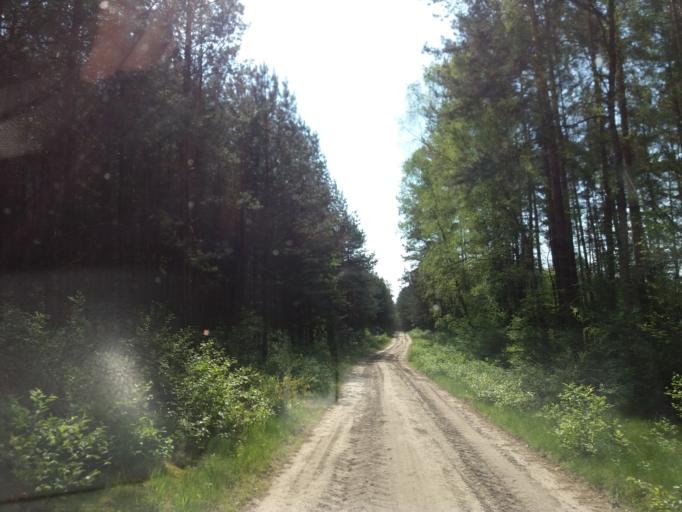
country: PL
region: West Pomeranian Voivodeship
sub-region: Powiat choszczenski
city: Bierzwnik
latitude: 53.1277
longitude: 15.6664
